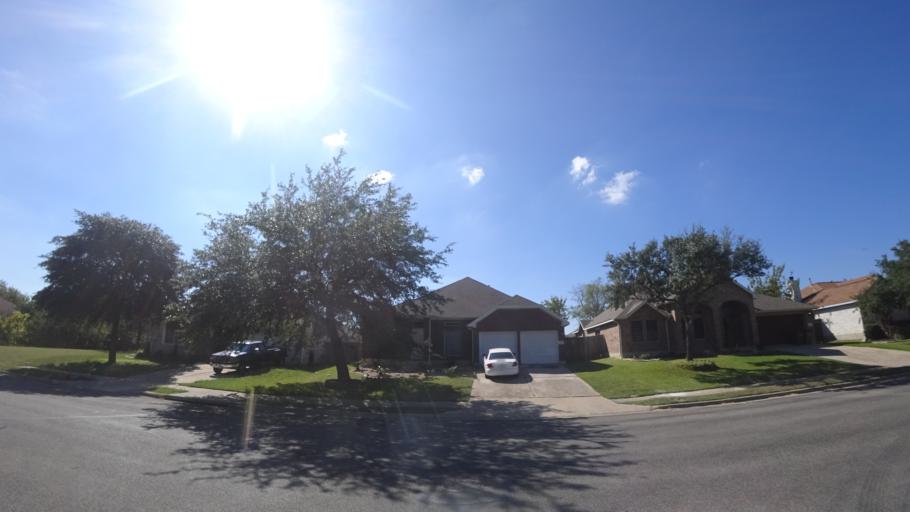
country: US
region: Texas
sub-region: Travis County
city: Manor
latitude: 30.3457
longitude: -97.6120
